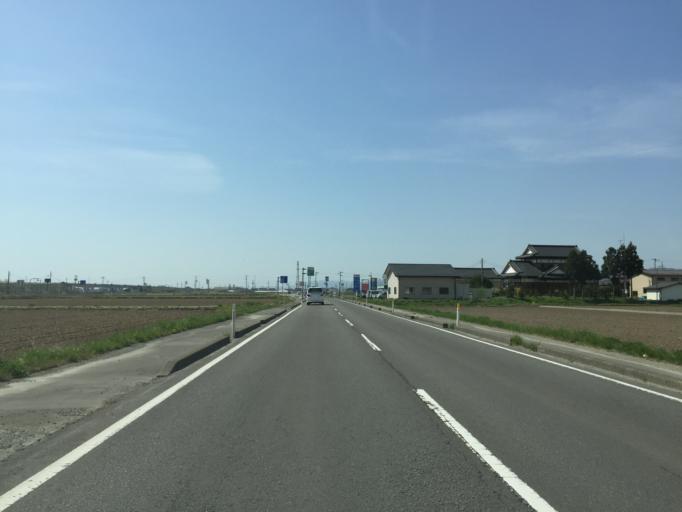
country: JP
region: Miyagi
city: Watari
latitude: 38.0403
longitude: 140.8899
